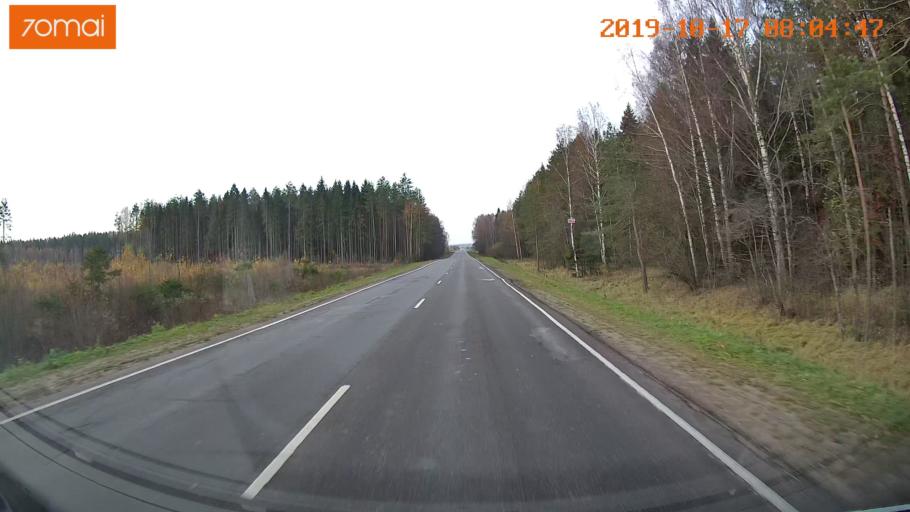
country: RU
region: Vladimir
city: Belaya Rechka
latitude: 56.3416
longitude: 39.4282
